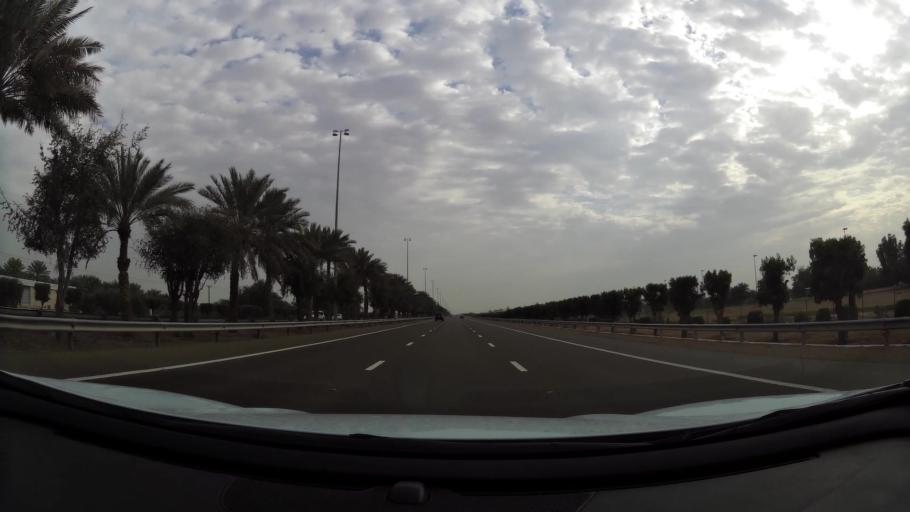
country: AE
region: Abu Dhabi
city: Al Ain
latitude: 24.1929
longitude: 55.3551
